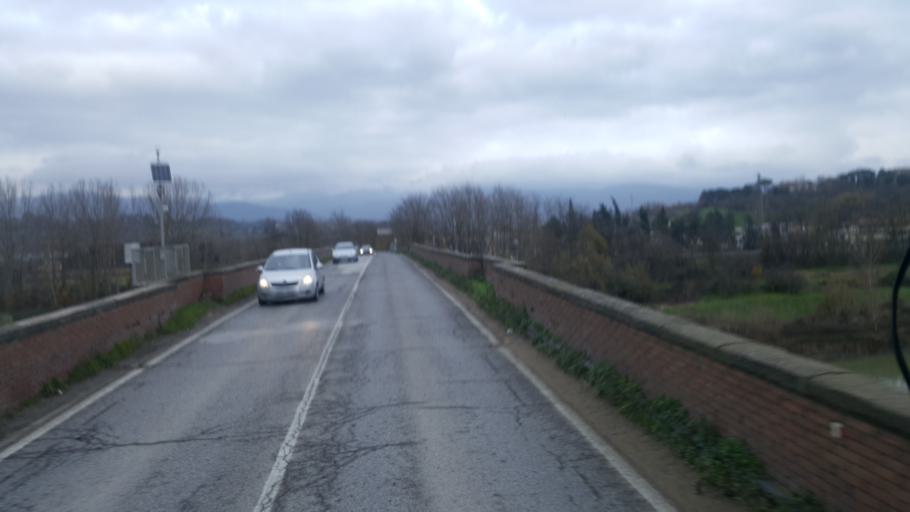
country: IT
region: Tuscany
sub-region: Province of Arezzo
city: Montevarchi
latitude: 43.5407
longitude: 11.5658
